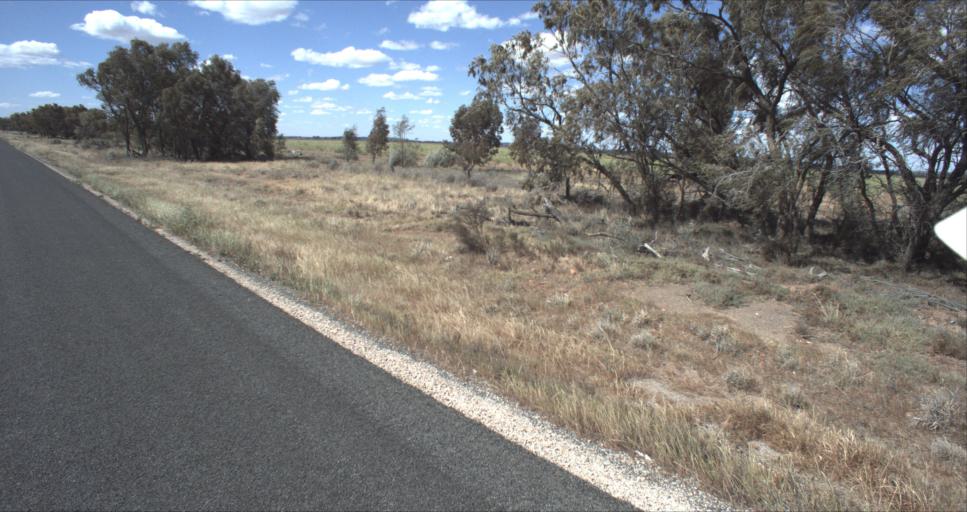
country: AU
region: New South Wales
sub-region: Leeton
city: Leeton
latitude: -34.4377
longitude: 146.2570
